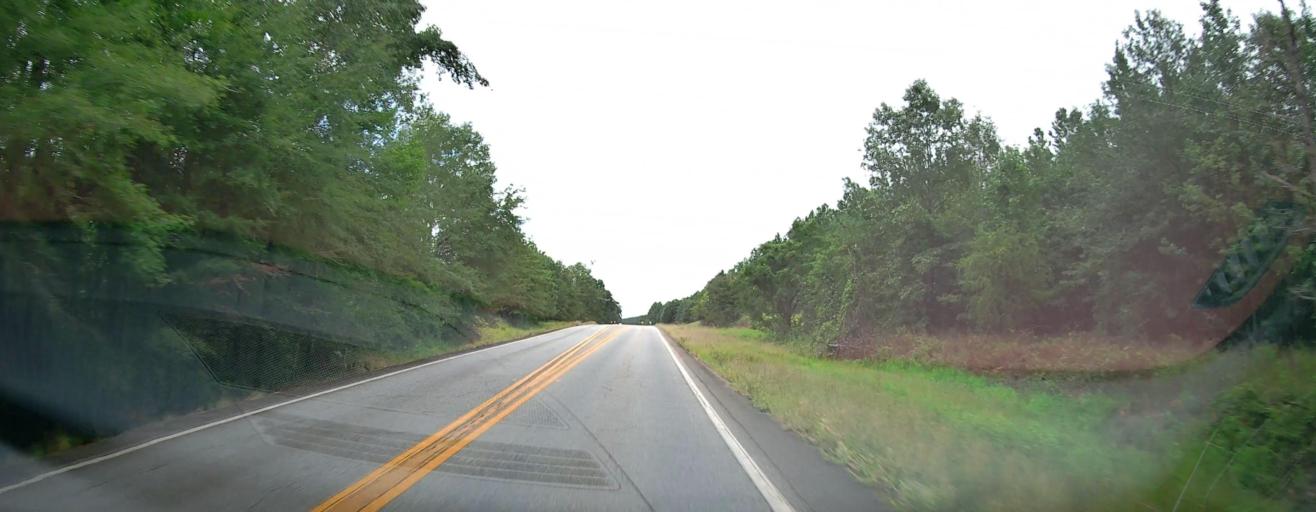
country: US
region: Georgia
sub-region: Marion County
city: Buena Vista
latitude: 32.2806
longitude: -84.4398
